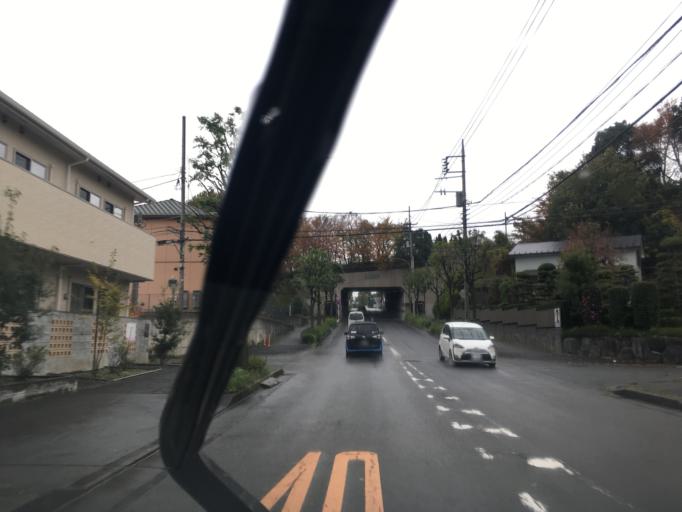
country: JP
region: Tokyo
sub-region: Machida-shi
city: Machida
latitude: 35.5769
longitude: 139.4082
